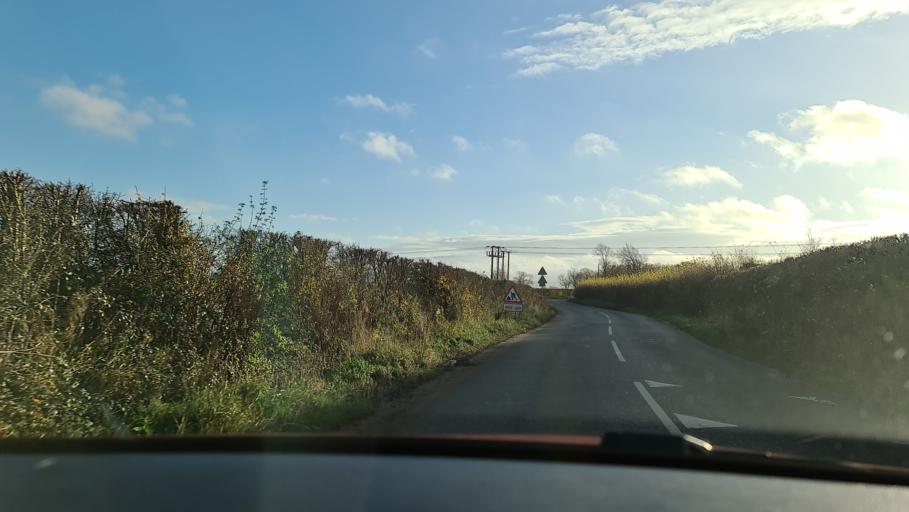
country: GB
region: England
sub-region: Buckinghamshire
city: Aylesbury
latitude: 51.7832
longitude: -0.8286
